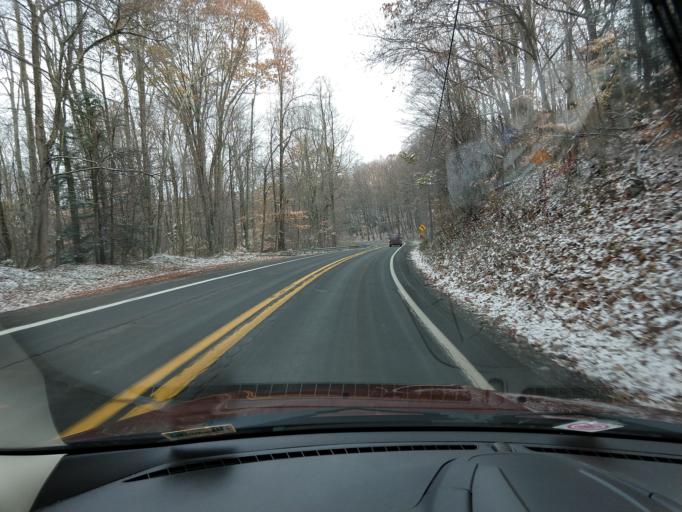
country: US
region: West Virginia
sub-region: Nicholas County
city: Craigsville
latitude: 38.2443
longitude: -80.7181
